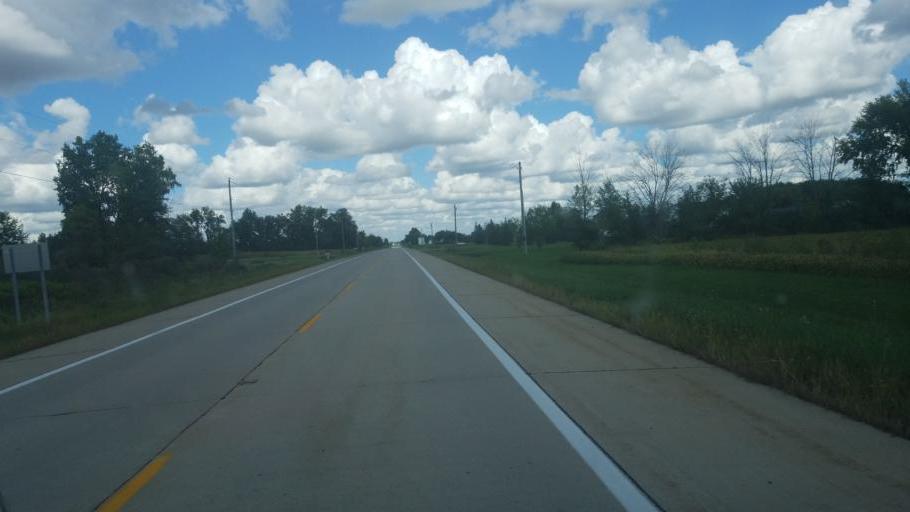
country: US
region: Ohio
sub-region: Champaign County
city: North Lewisburg
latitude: 40.3108
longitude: -83.5041
